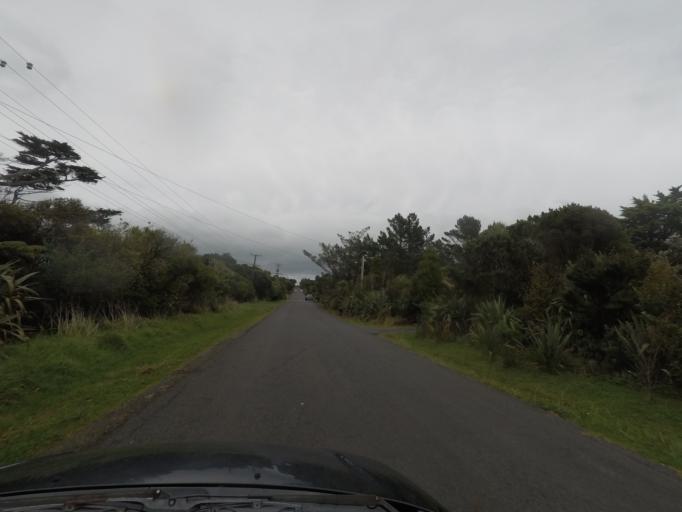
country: NZ
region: Auckland
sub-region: Auckland
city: Muriwai Beach
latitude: -36.9673
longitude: 174.4780
